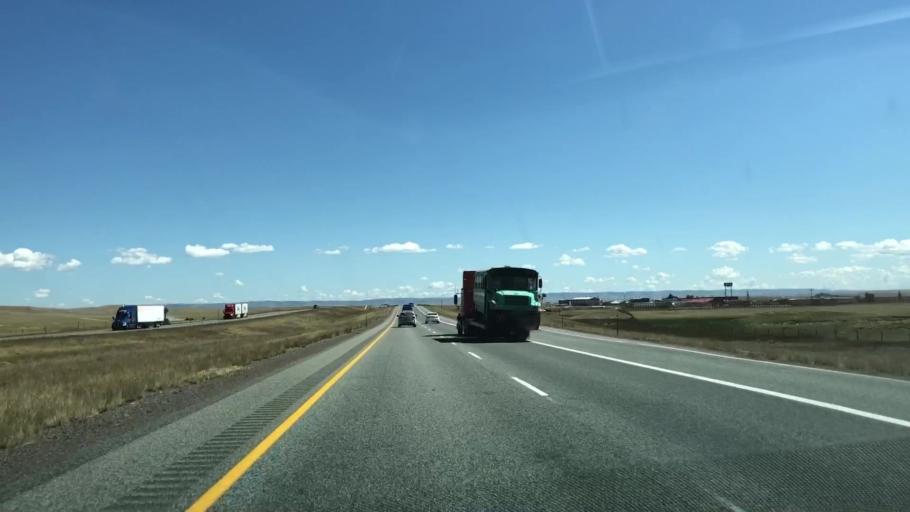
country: US
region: Wyoming
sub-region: Albany County
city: Laramie
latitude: 41.4414
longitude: -105.9497
